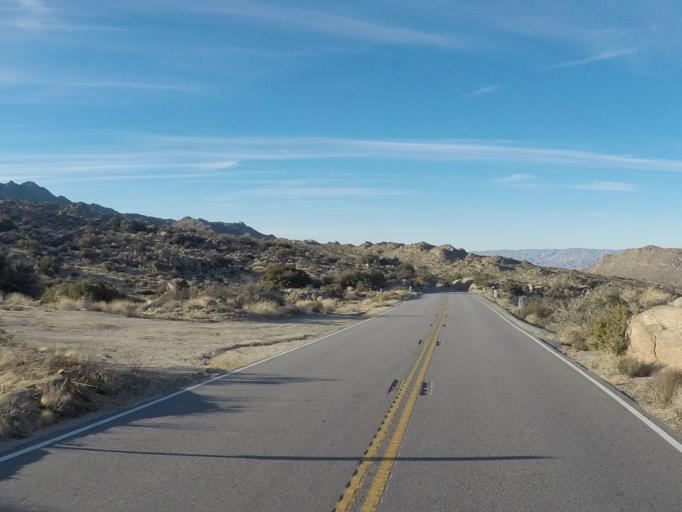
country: US
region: California
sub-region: Riverside County
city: La Quinta
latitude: 33.6037
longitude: -116.4191
